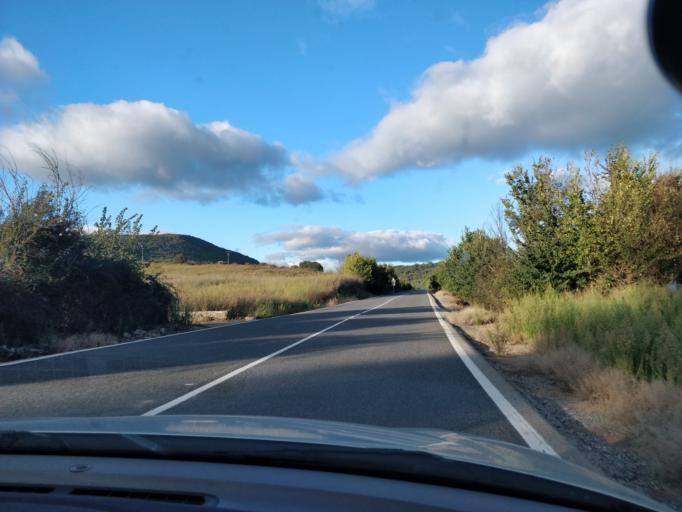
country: ES
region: Castille and Leon
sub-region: Provincia de Leon
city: Borrenes
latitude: 42.4940
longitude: -6.7405
